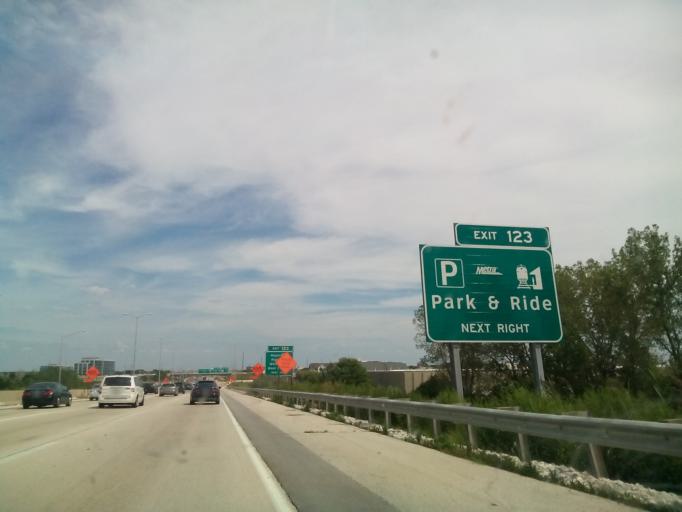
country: US
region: Illinois
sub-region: DuPage County
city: Warrenville
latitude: 41.8027
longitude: -88.2135
